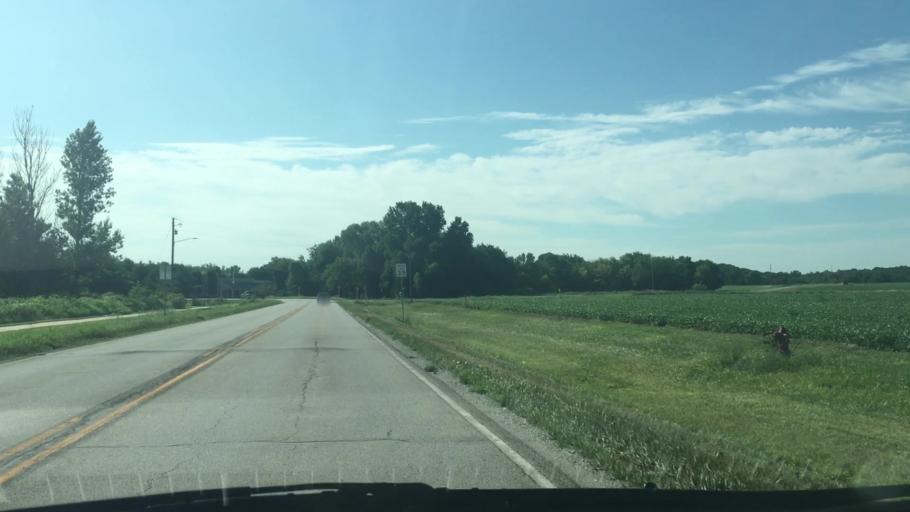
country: US
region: Iowa
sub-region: Johnson County
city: North Liberty
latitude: 41.7352
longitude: -91.5815
